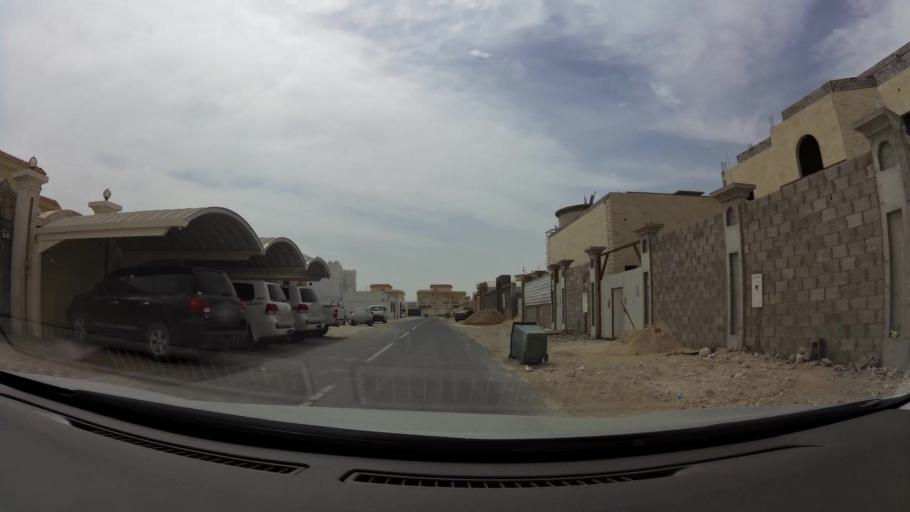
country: QA
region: Baladiyat ad Dawhah
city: Doha
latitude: 25.2105
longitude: 51.4695
